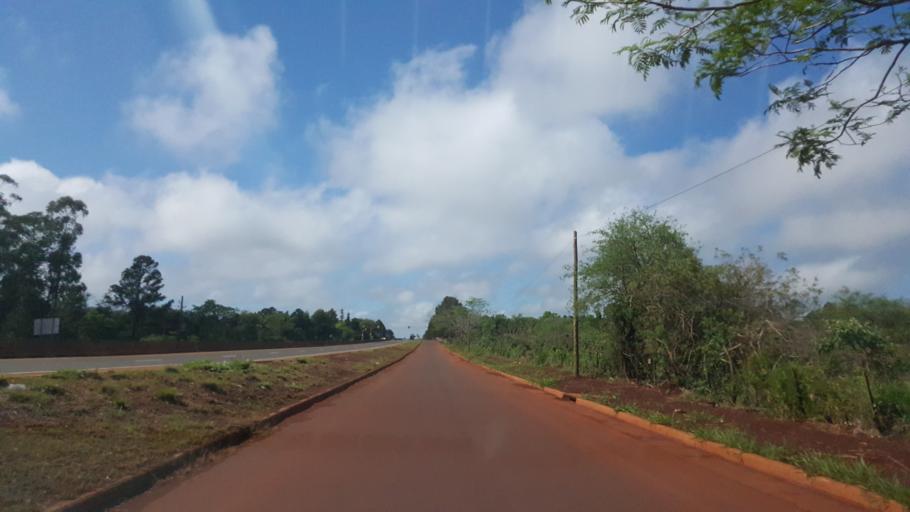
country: AR
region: Misiones
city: Garupa
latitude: -27.4923
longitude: -55.8645
